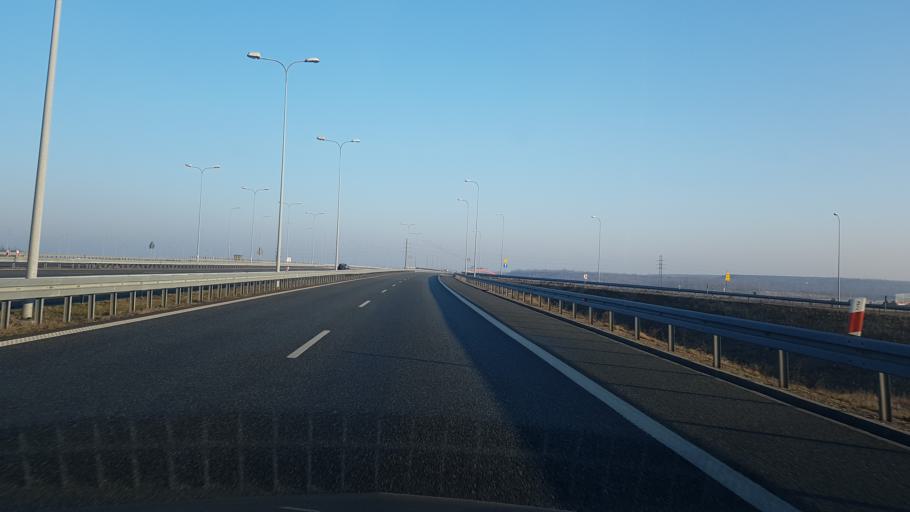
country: PL
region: Silesian Voivodeship
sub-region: Powiat gliwicki
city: Przyszowice
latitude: 50.2587
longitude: 18.7189
